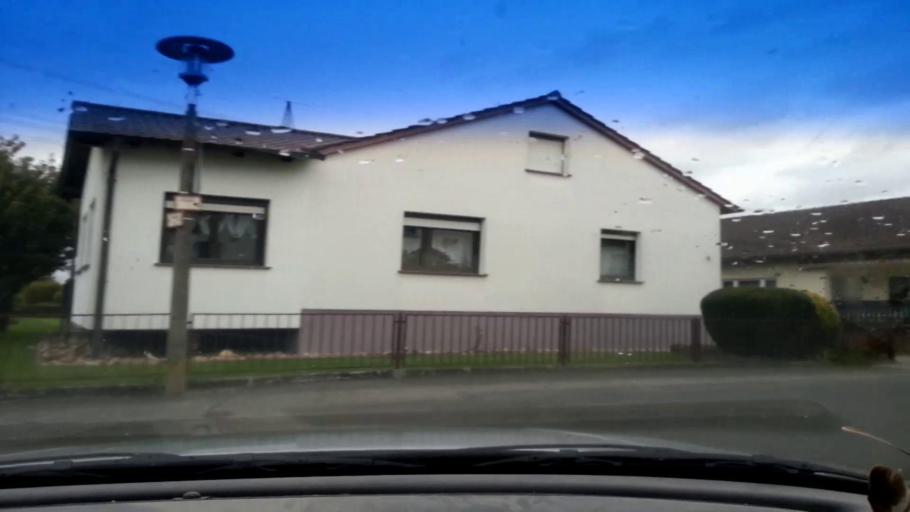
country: DE
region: Bavaria
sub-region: Upper Franconia
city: Hallstadt
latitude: 49.9319
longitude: 10.8696
